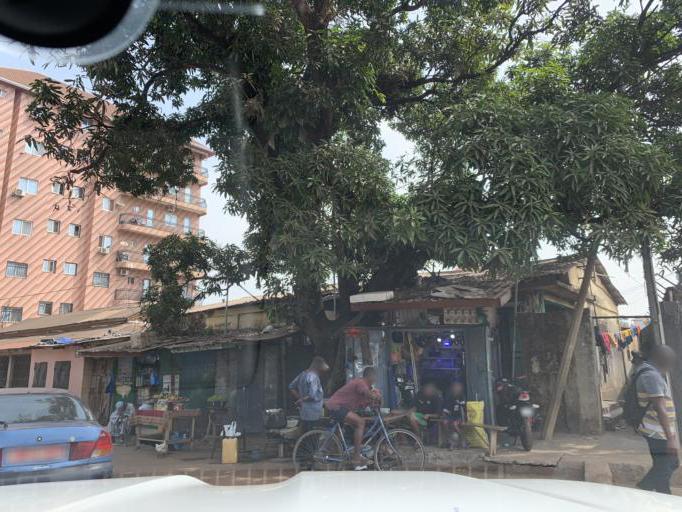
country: GN
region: Conakry
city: Conakry
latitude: 9.5495
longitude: -13.6706
